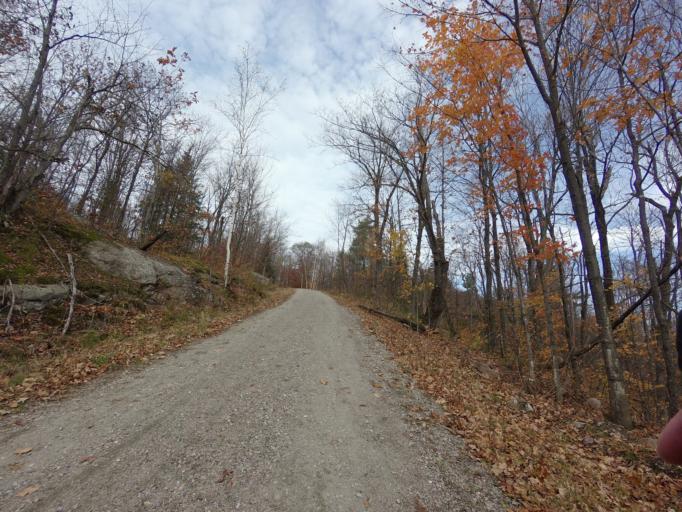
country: CA
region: Quebec
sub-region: Outaouais
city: Wakefield
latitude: 45.5336
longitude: -75.9435
